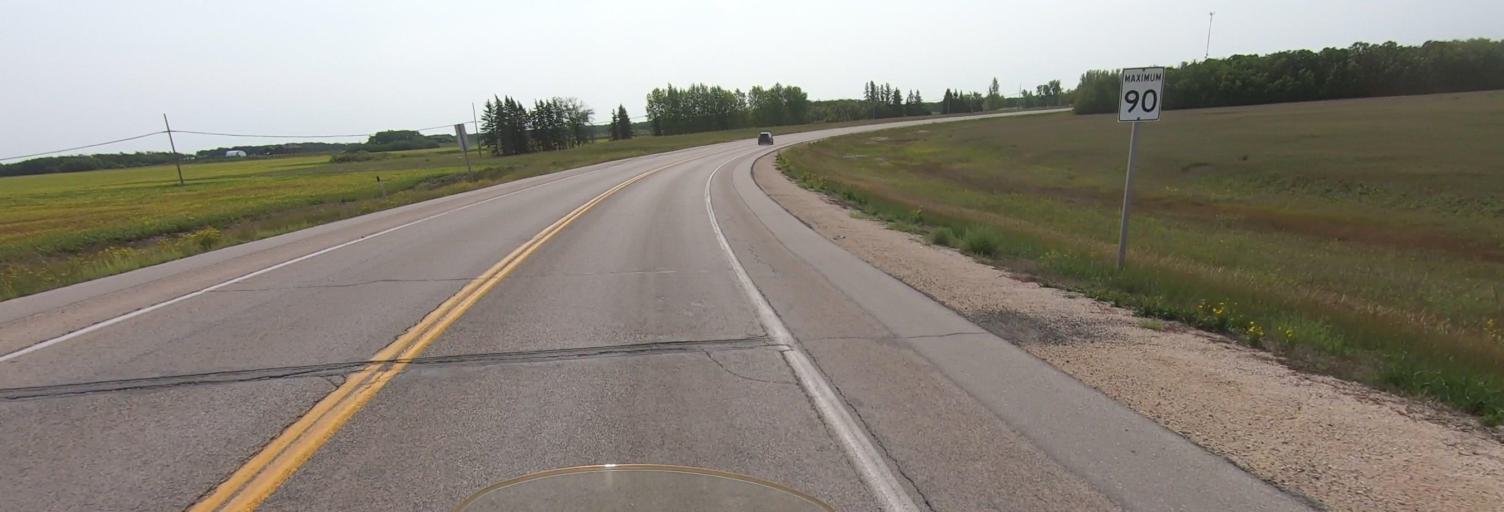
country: CA
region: Manitoba
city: Winnipeg
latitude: 49.7547
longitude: -97.1168
